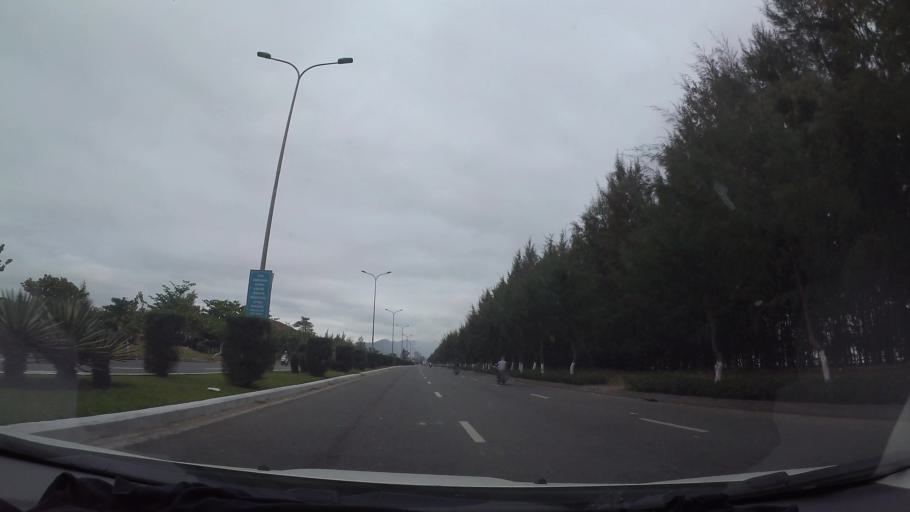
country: VN
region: Da Nang
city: Lien Chieu
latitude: 16.0939
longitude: 108.1475
